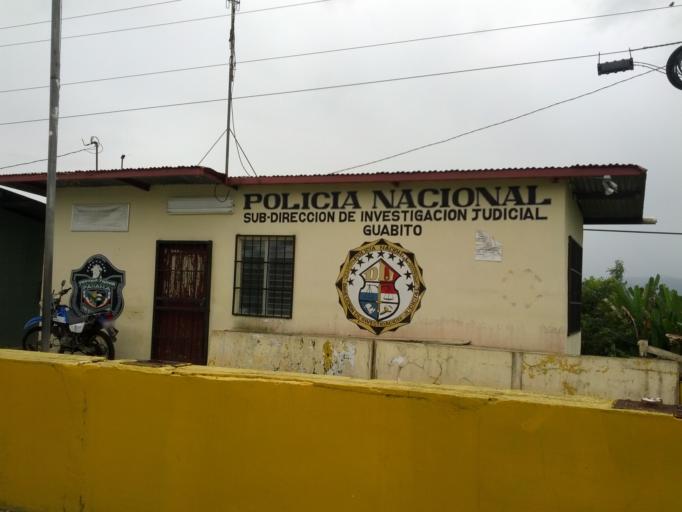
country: PA
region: Bocas del Toro
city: Guabito
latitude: 9.4988
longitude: -82.6133
